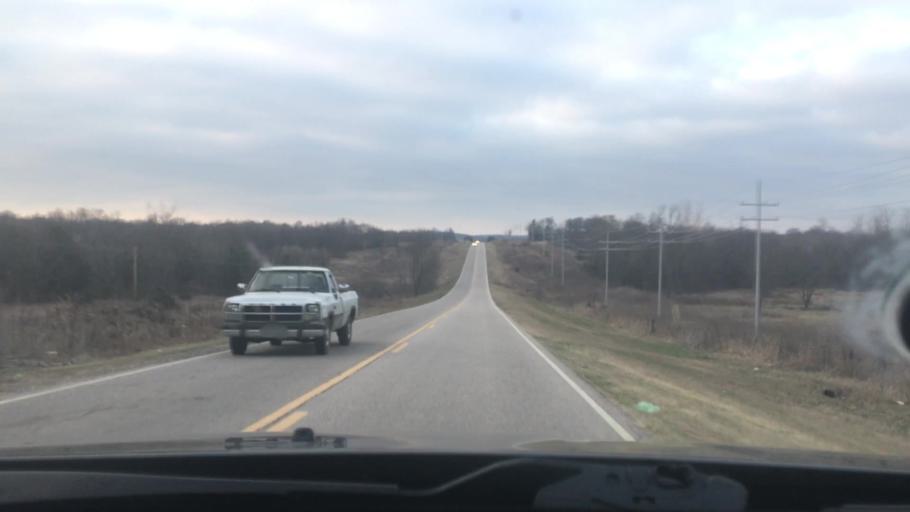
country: US
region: Oklahoma
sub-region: Pontotoc County
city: Ada
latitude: 34.6293
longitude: -96.6349
